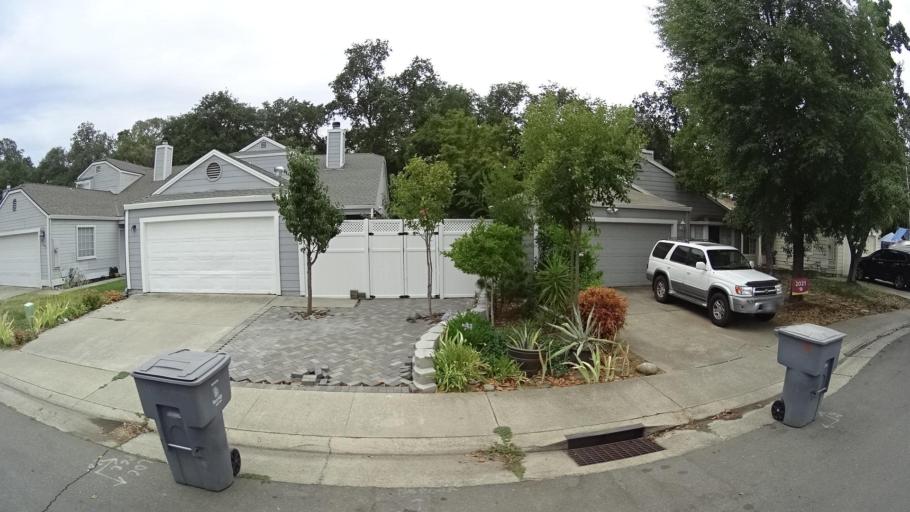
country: US
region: California
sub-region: Placer County
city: Rocklin
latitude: 38.7756
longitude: -121.2522
